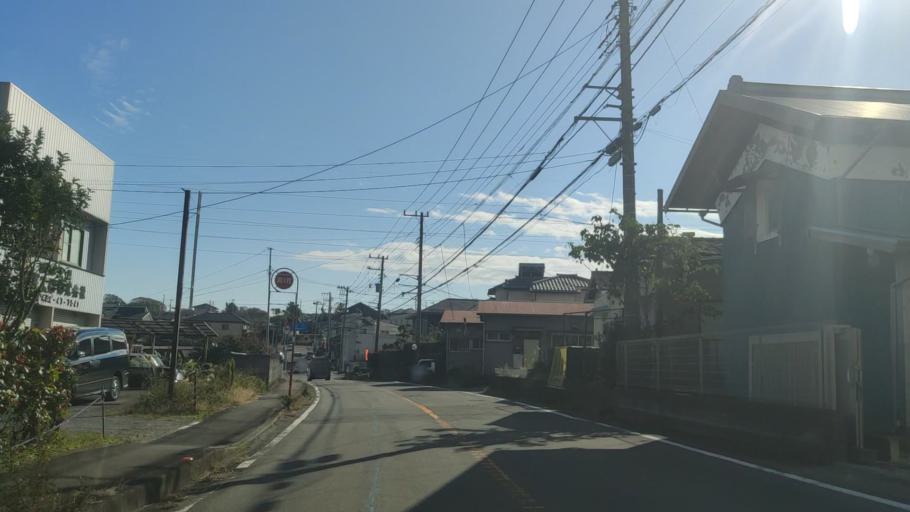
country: JP
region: Kanagawa
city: Atsugi
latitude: 35.4395
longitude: 139.3400
